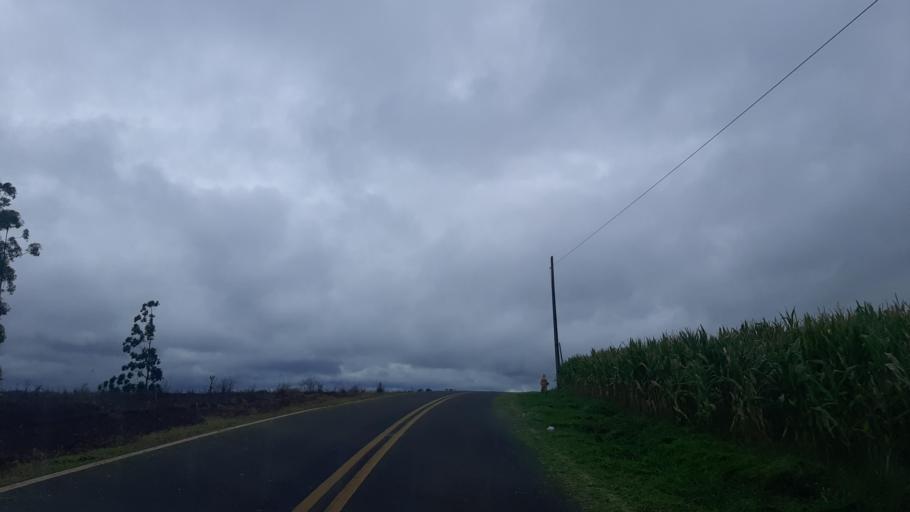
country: BR
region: Parana
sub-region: Ampere
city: Ampere
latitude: -25.9567
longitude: -53.4489
